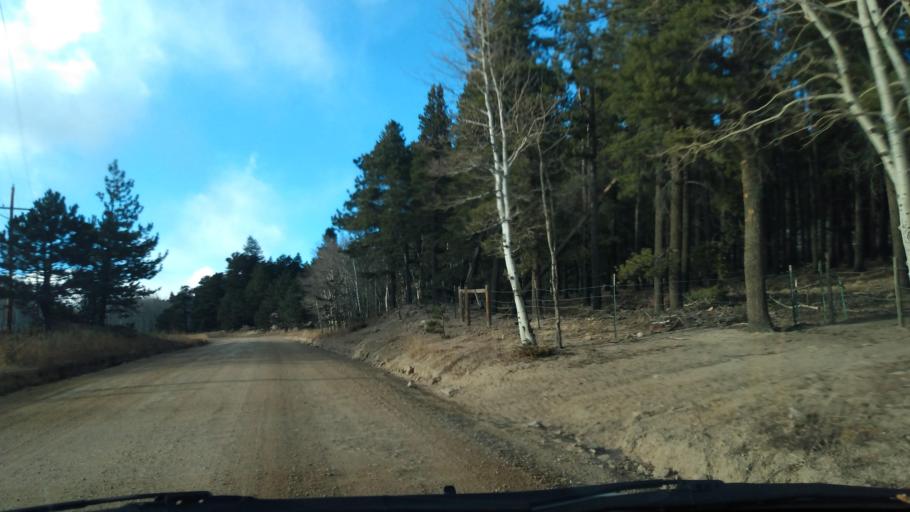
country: US
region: Colorado
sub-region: Boulder County
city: Nederland
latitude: 39.9525
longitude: -105.4552
